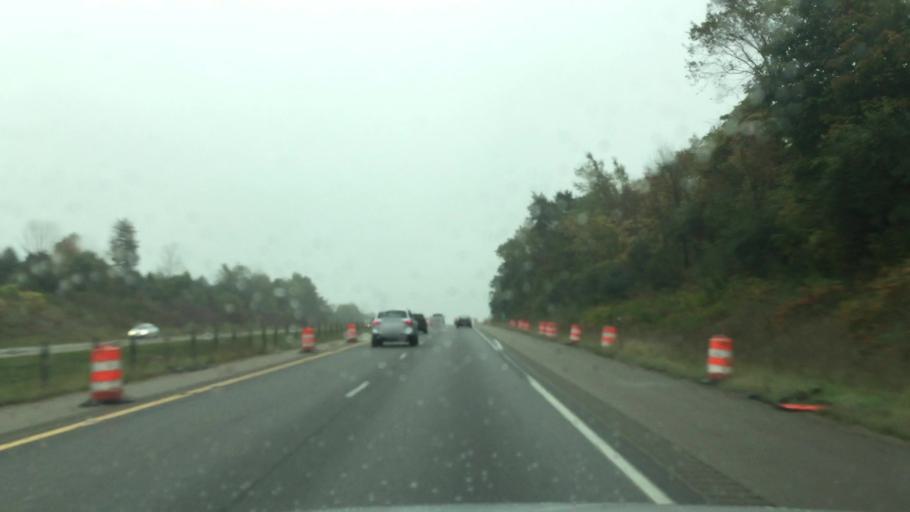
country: US
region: Michigan
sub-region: Van Buren County
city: Hartford
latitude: 42.1973
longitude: -86.0949
